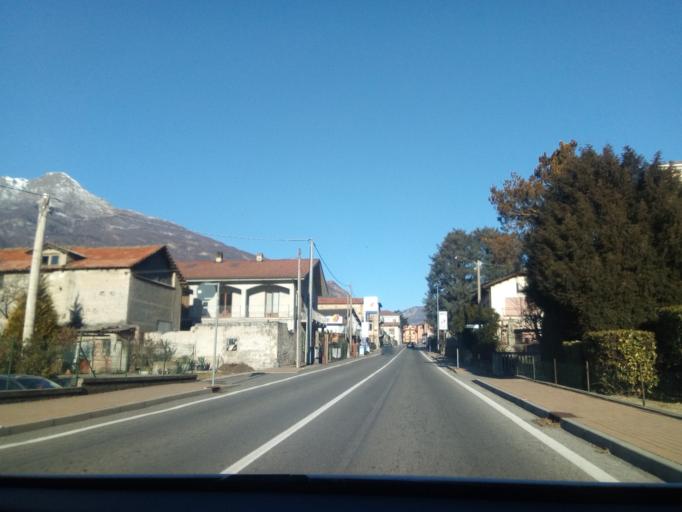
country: IT
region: Piedmont
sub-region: Provincia di Torino
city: Settimo Vittone
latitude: 45.5442
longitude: 7.8355
